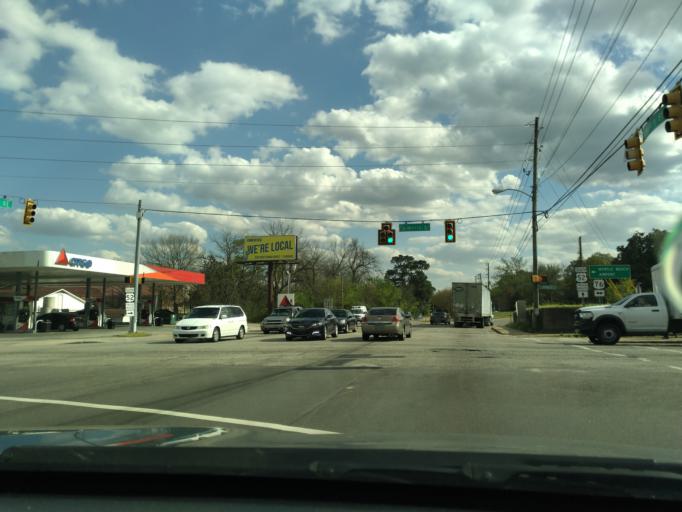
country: US
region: South Carolina
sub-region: Florence County
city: Florence
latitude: 34.1942
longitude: -79.7618
